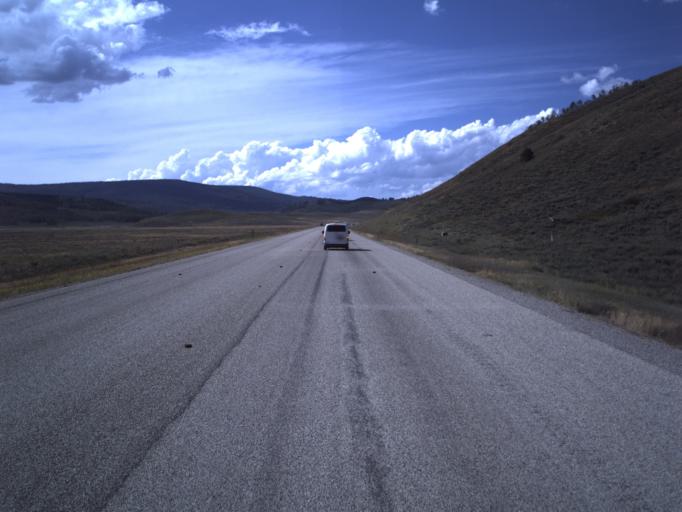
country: US
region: Utah
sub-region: Wasatch County
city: Heber
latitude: 40.2579
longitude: -111.2027
